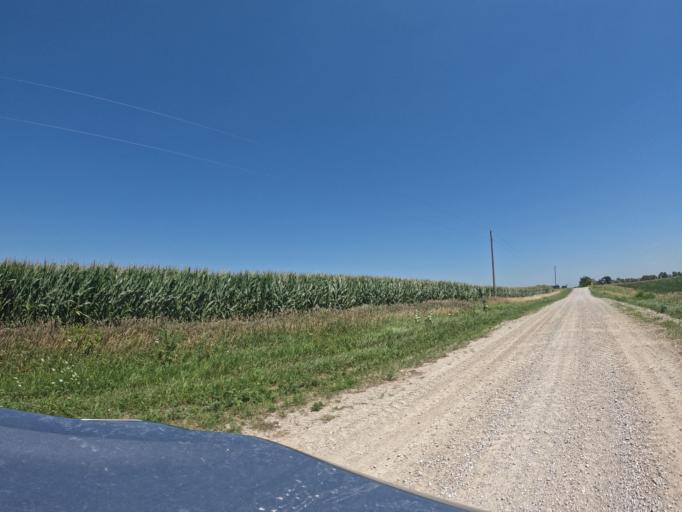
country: US
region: Iowa
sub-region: Keokuk County
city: Sigourney
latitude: 41.4235
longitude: -92.3180
